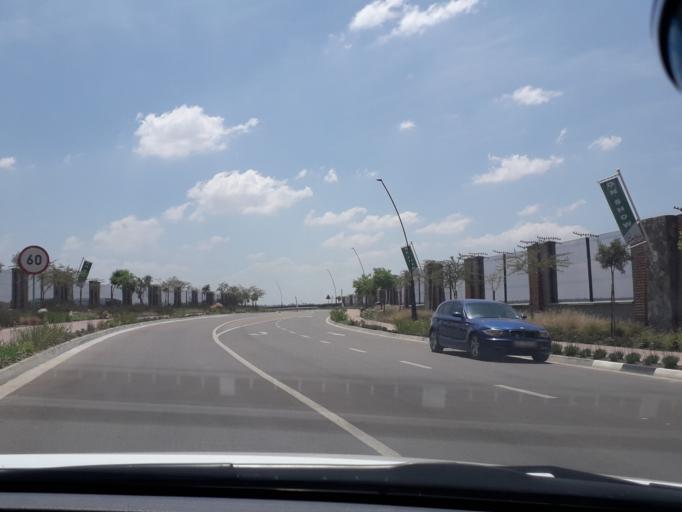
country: ZA
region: Gauteng
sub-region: City of Johannesburg Metropolitan Municipality
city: Midrand
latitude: -26.0266
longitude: 28.0871
